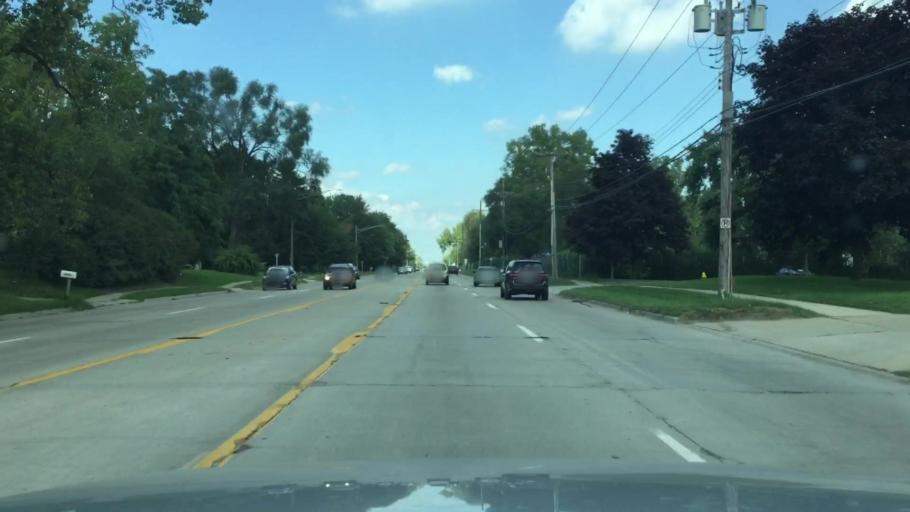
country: US
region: Michigan
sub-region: Wayne County
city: Wayne
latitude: 42.2701
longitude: -83.3480
